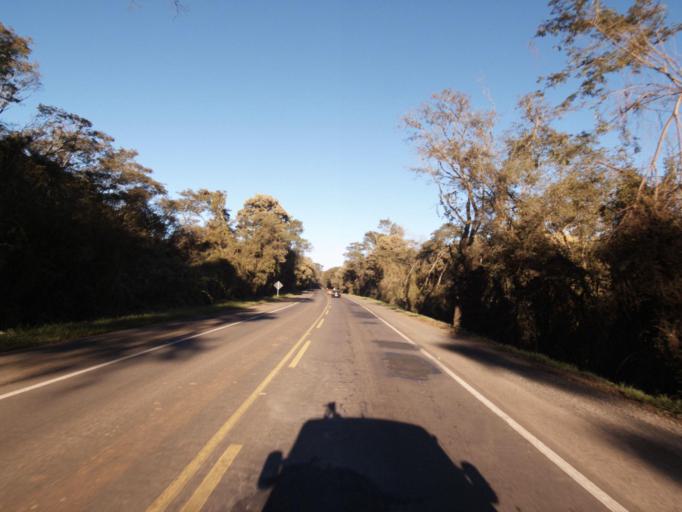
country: BR
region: Santa Catarina
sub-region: Sao Lourenco Do Oeste
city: Sao Lourenco dOeste
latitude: -26.7663
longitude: -53.2587
